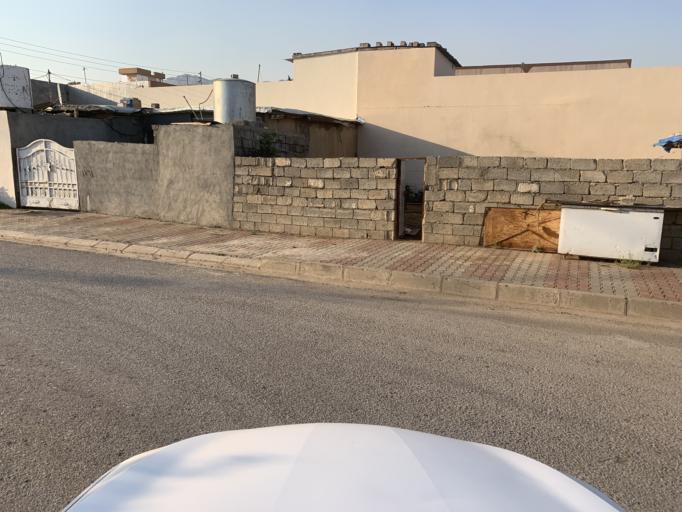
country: IQ
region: As Sulaymaniyah
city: Raniye
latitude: 36.2375
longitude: 44.8815
